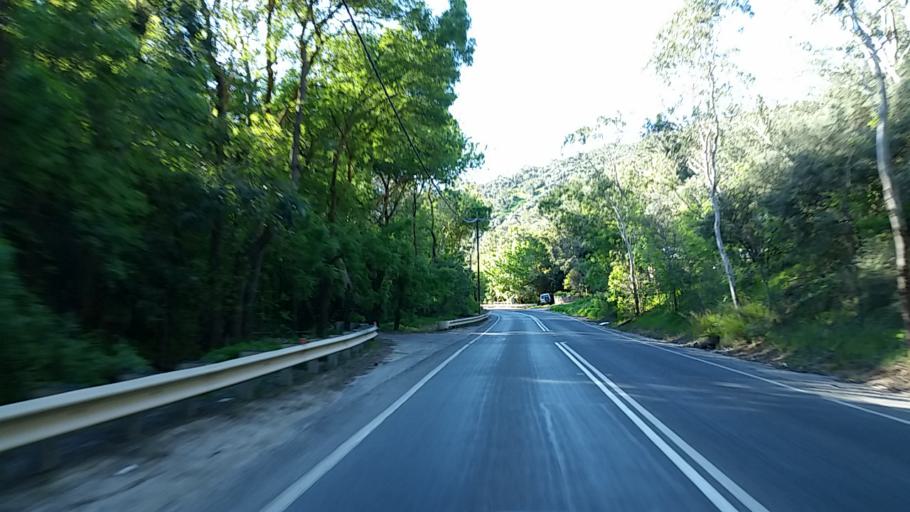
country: AU
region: South Australia
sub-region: Adelaide Hills
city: Adelaide Hills
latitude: -34.9187
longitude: 138.6954
